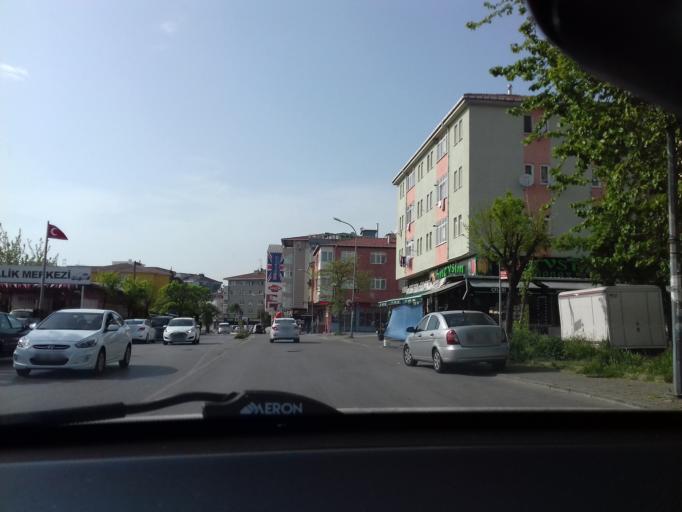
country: TR
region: Istanbul
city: Maltepe
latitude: 40.9146
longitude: 29.2080
